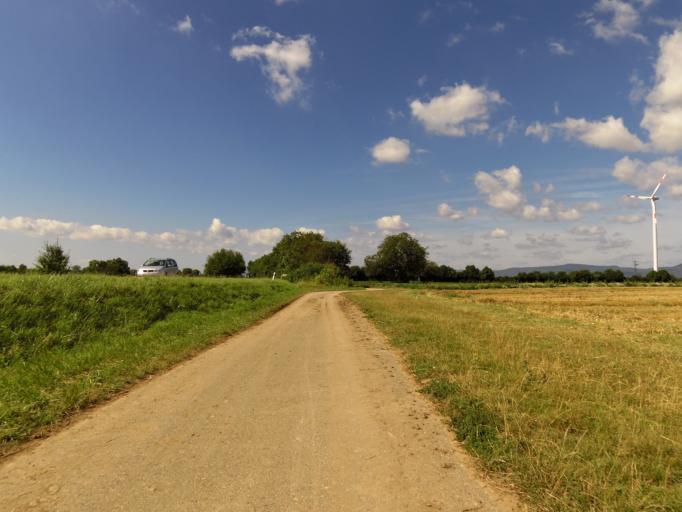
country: DE
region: Rheinland-Pfalz
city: Bohl-Iggelheim
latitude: 49.3814
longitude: 8.2774
